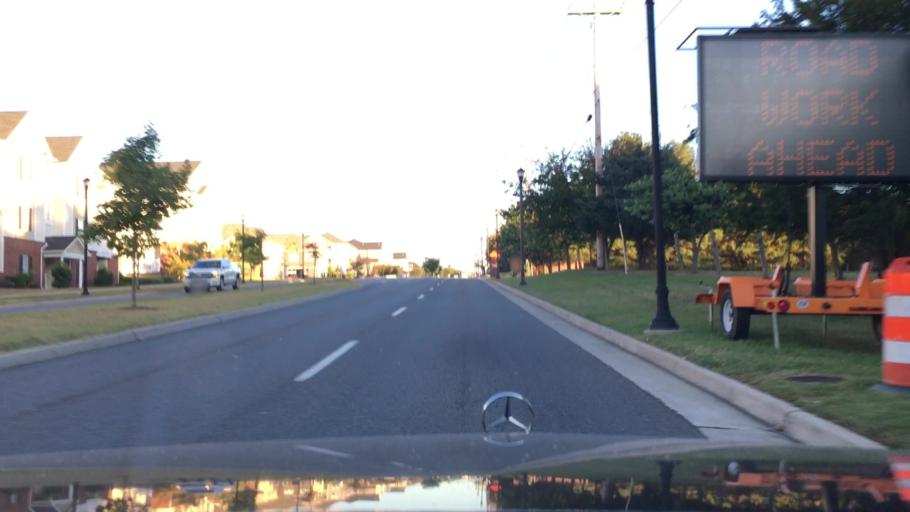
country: US
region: Virginia
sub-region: Campbell County
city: Timberlake
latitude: 37.3408
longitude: -79.2289
